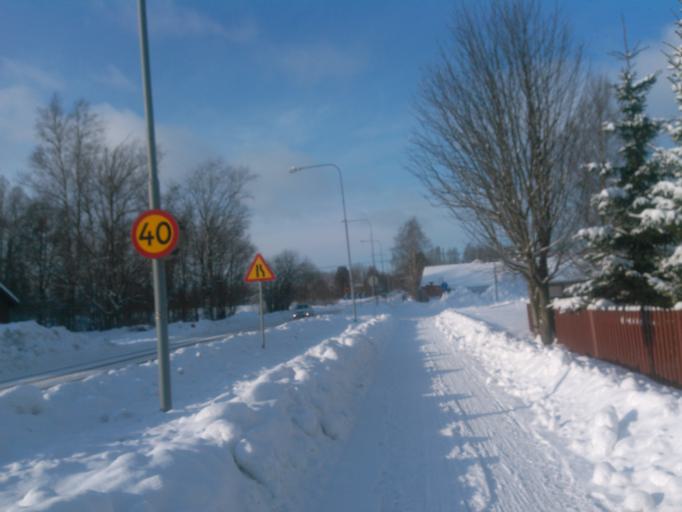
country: SE
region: Vaesterbotten
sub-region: Umea Kommun
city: Umea
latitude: 63.8072
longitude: 20.2733
